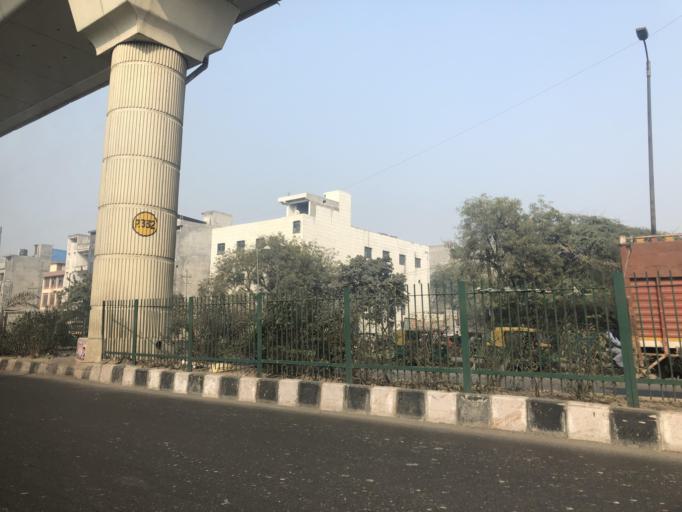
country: IN
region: NCT
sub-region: West Delhi
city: Nangloi Jat
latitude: 28.6811
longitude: 77.0802
